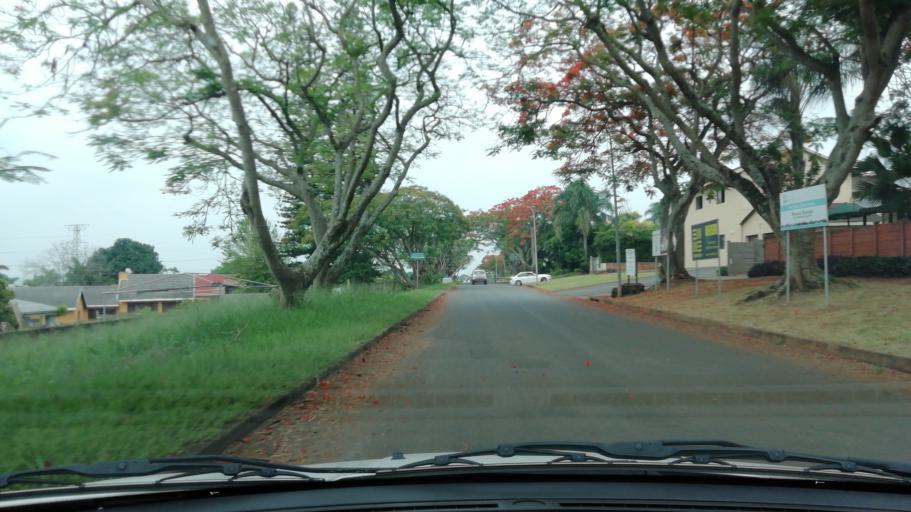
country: ZA
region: KwaZulu-Natal
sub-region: uThungulu District Municipality
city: Empangeni
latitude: -28.7391
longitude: 31.8888
